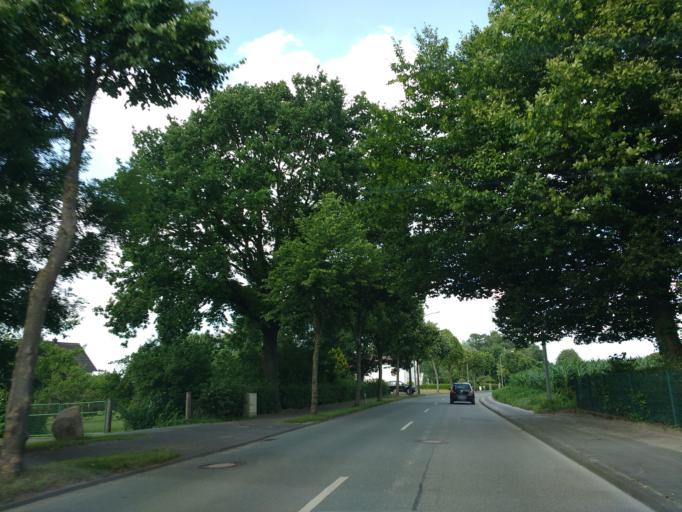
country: DE
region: North Rhine-Westphalia
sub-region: Regierungsbezirk Detmold
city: Salzkotten
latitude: 51.7166
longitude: 8.6707
